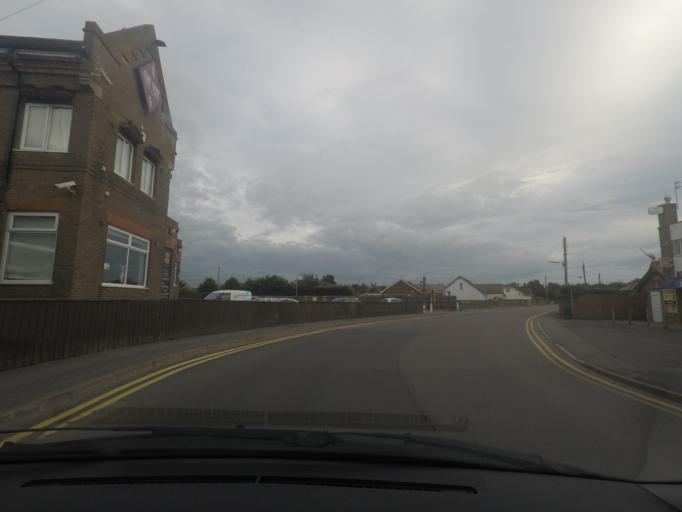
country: GB
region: England
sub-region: Lincolnshire
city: Chapel Saint Leonards
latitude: 53.2233
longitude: 0.3366
